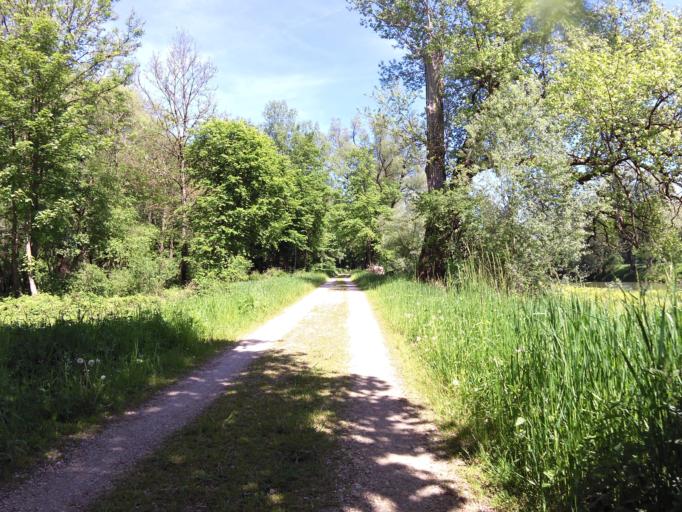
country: DE
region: Bavaria
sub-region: Upper Bavaria
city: Marzling
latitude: 48.4065
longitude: 11.8189
